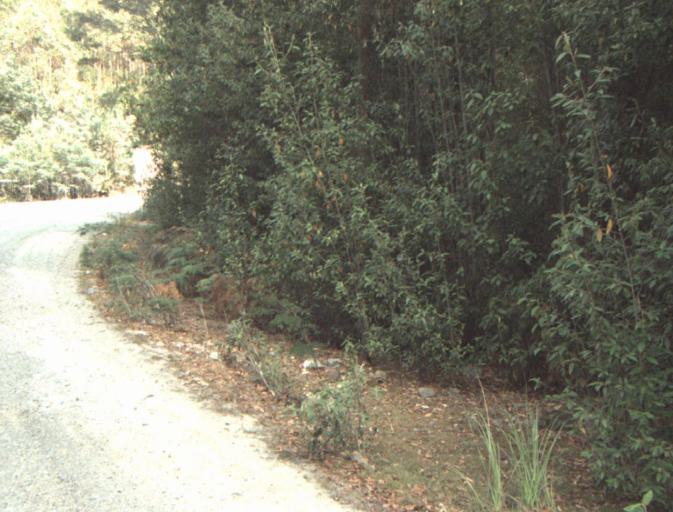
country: AU
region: Tasmania
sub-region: Launceston
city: Mayfield
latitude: -41.1940
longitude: 147.1600
